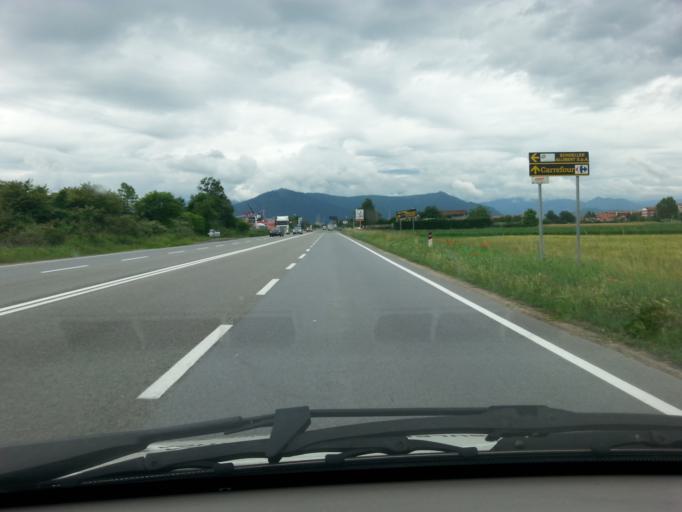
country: IT
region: Piedmont
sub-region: Provincia di Torino
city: Orbassano
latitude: 44.9955
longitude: 7.5409
